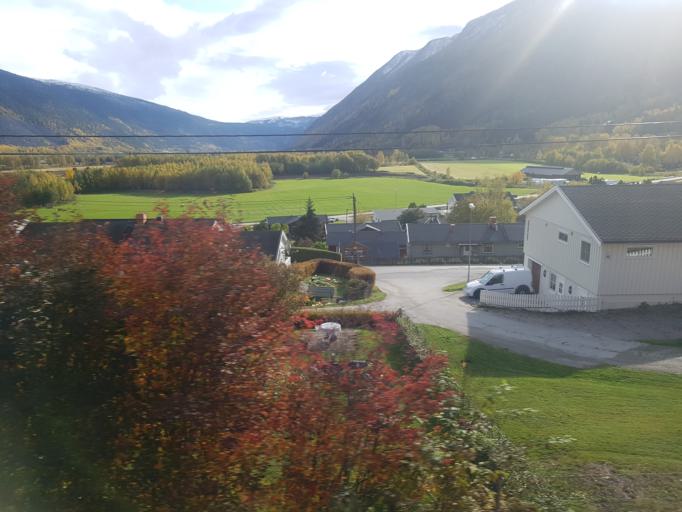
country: NO
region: Oppland
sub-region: Sel
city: Otta
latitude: 61.8432
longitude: 9.4001
